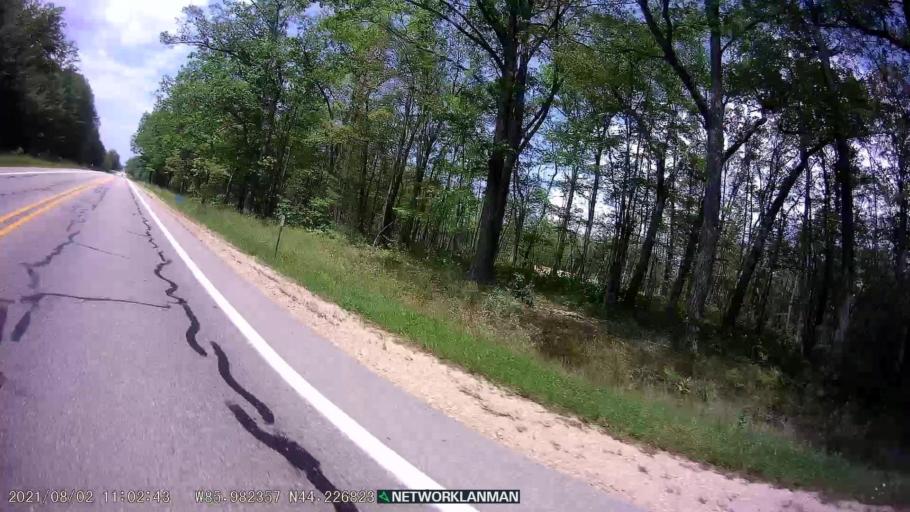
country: US
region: Michigan
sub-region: Manistee County
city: Manistee
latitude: 44.2269
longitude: -85.9828
